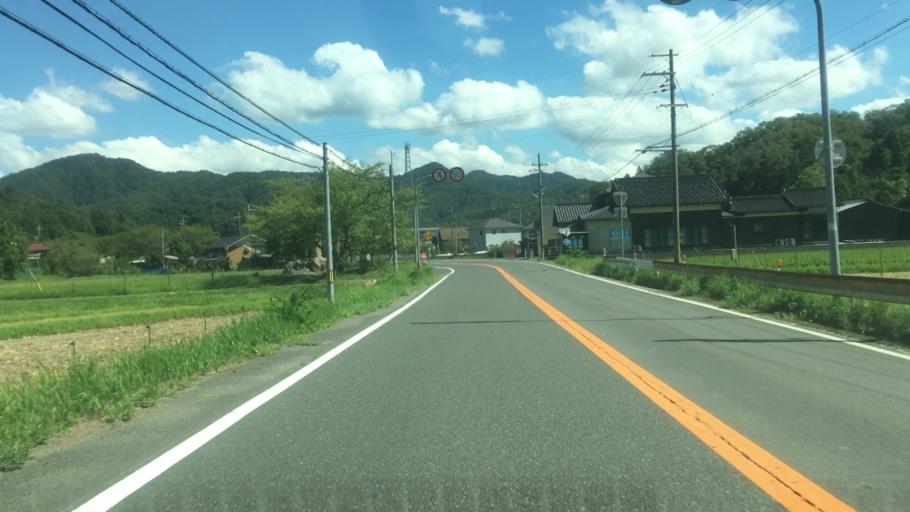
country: JP
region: Hyogo
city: Toyooka
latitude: 35.5798
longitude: 134.9703
